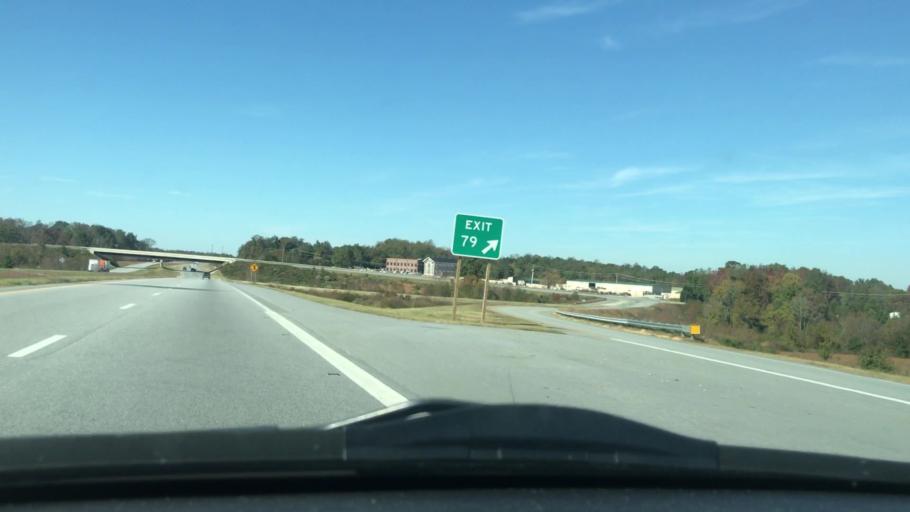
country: US
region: North Carolina
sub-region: Randolph County
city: Archdale
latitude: 35.8714
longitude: -79.8985
